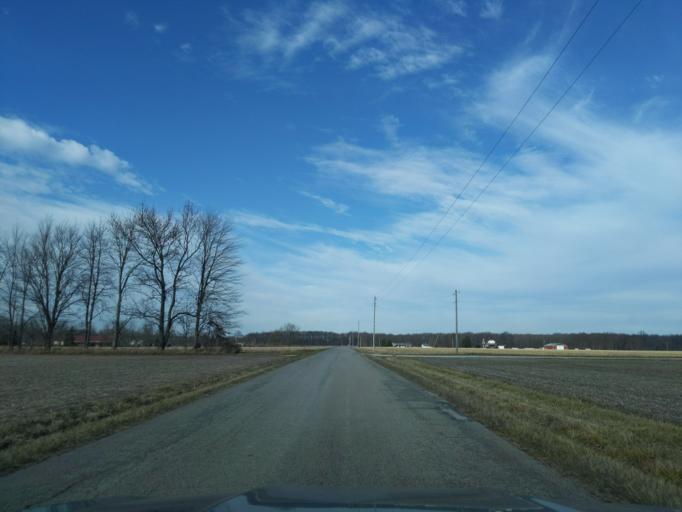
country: US
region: Indiana
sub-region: Decatur County
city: Greensburg
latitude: 39.2593
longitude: -85.4189
